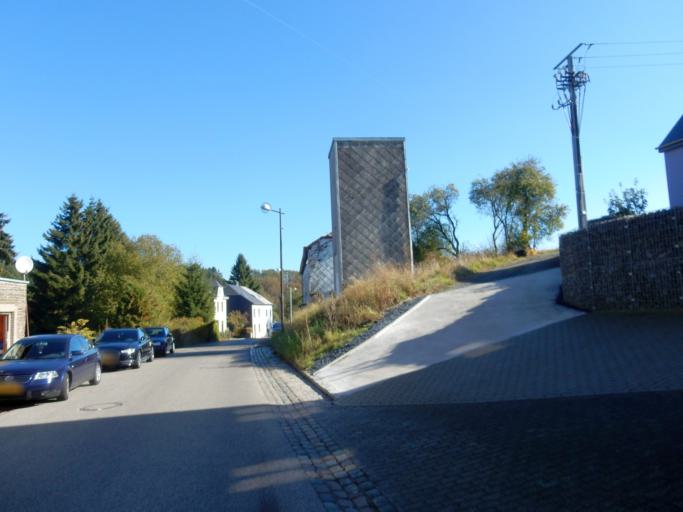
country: LU
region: Diekirch
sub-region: Canton de Clervaux
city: Troisvierges
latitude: 50.1194
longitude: 5.9865
